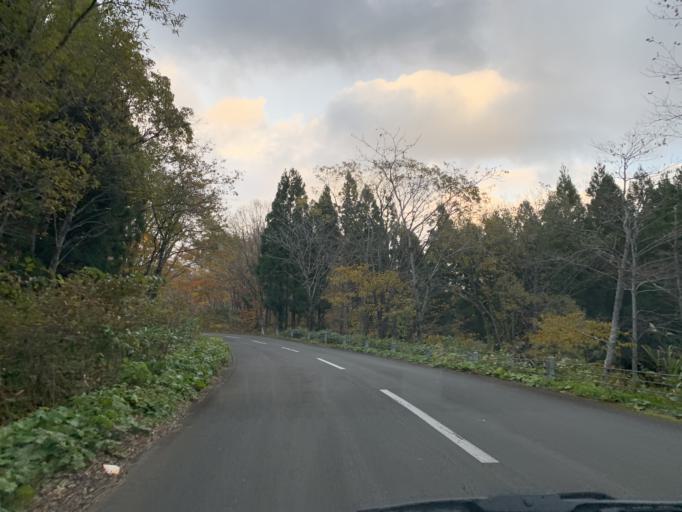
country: JP
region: Iwate
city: Mizusawa
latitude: 39.1120
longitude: 140.8789
